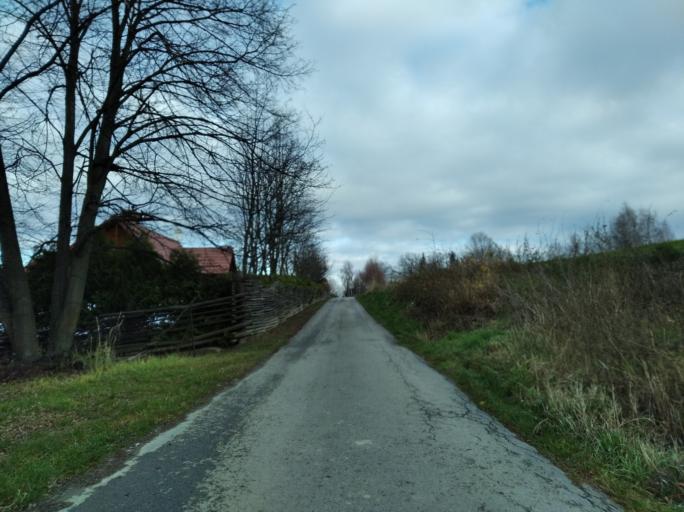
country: PL
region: Subcarpathian Voivodeship
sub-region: Powiat strzyzowski
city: Polomia
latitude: 49.8844
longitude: 21.8483
